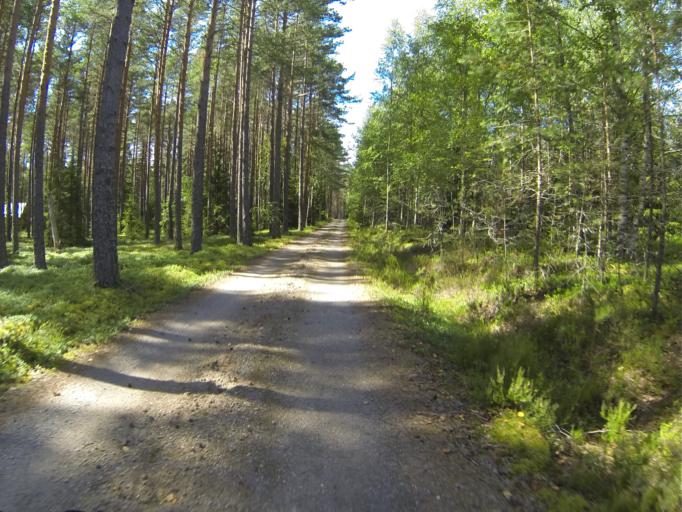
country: FI
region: Varsinais-Suomi
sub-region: Salo
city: Pernioe
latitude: 60.2802
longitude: 23.0378
